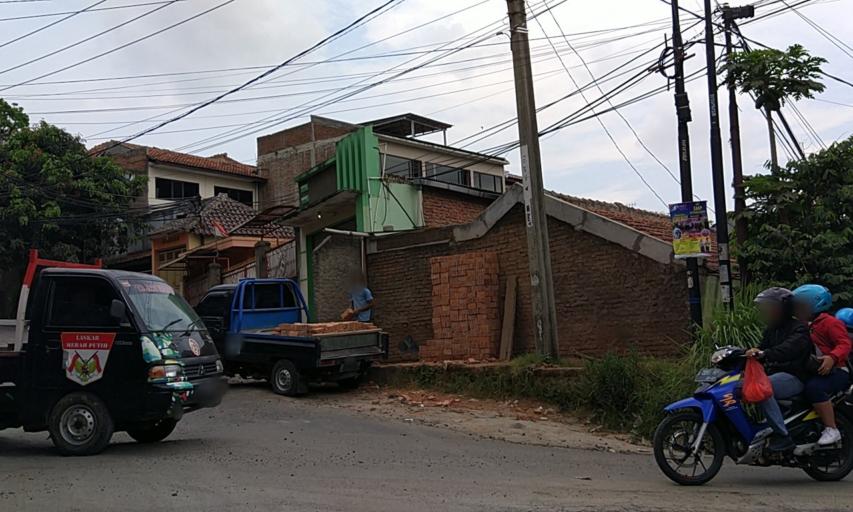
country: ID
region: West Java
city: Cileunyi
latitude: -6.9001
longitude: 107.6971
